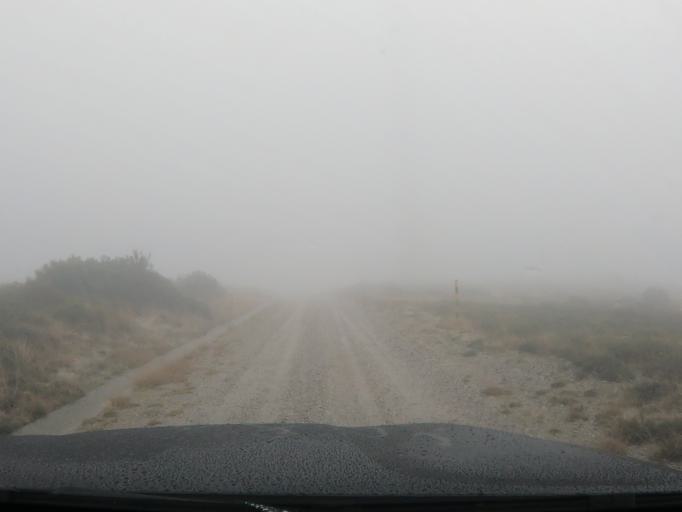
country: PT
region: Vila Real
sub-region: Vila Real
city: Vila Real
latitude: 41.3336
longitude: -7.8483
